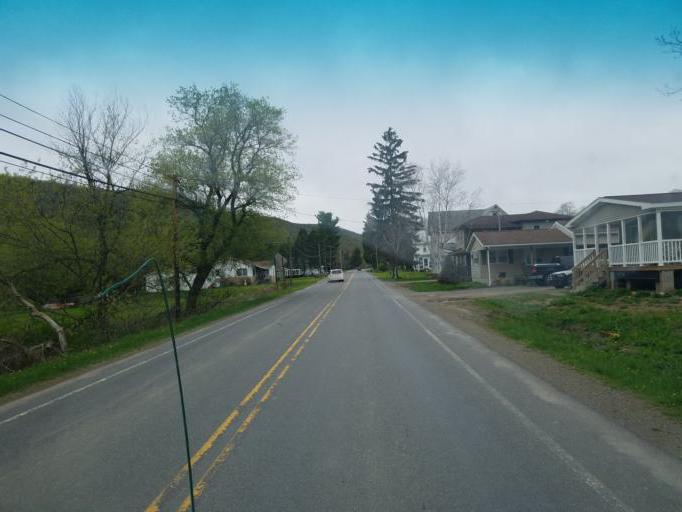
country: US
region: Pennsylvania
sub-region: Tioga County
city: Westfield
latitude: 41.9418
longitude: -77.6517
